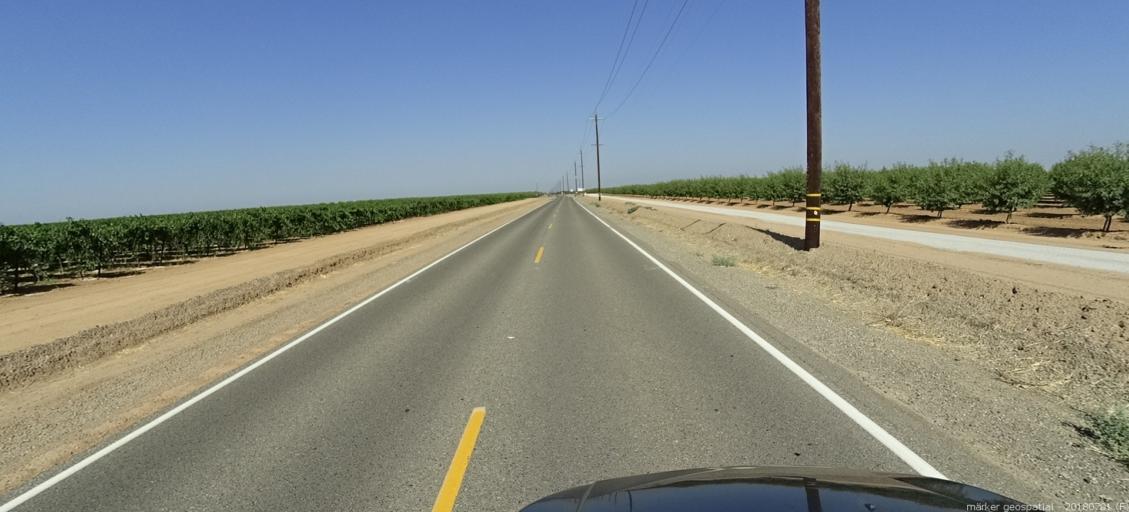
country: US
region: California
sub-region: Madera County
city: Bonadelle Ranchos-Madera Ranchos
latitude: 36.8804
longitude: -119.8361
